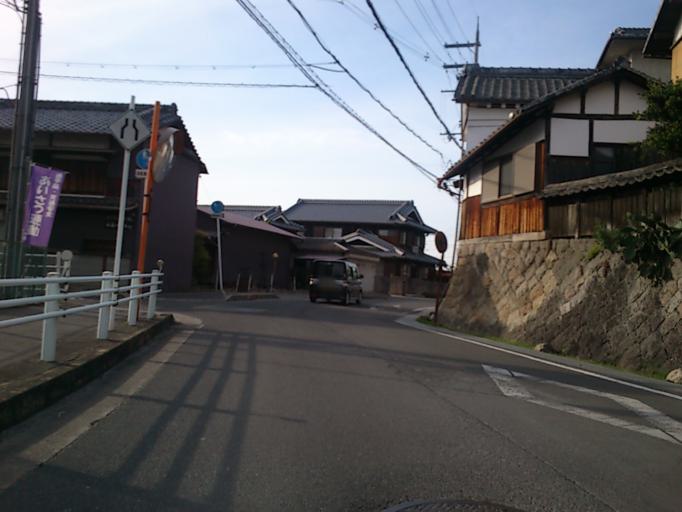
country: JP
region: Nara
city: Nara-shi
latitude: 34.7573
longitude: 135.8171
